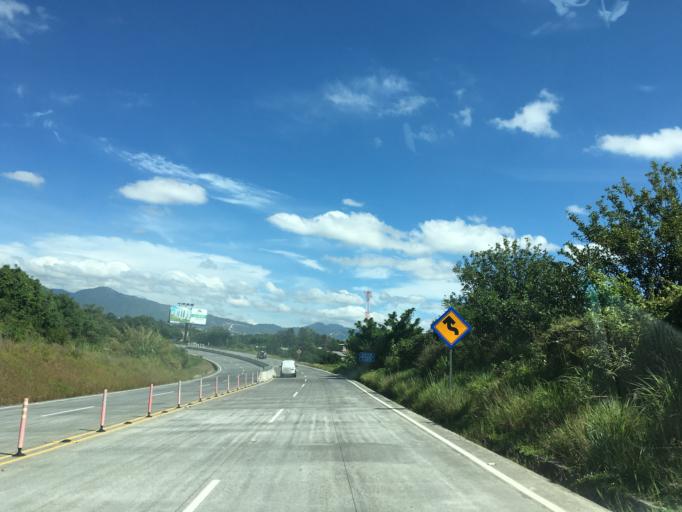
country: GT
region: Guatemala
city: Petapa
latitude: 14.4882
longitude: -90.5547
